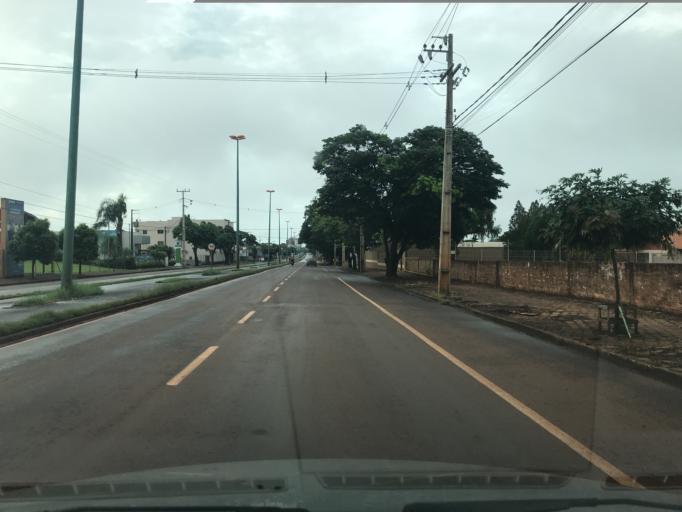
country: BR
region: Parana
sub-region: Palotina
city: Palotina
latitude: -24.2955
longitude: -53.8359
